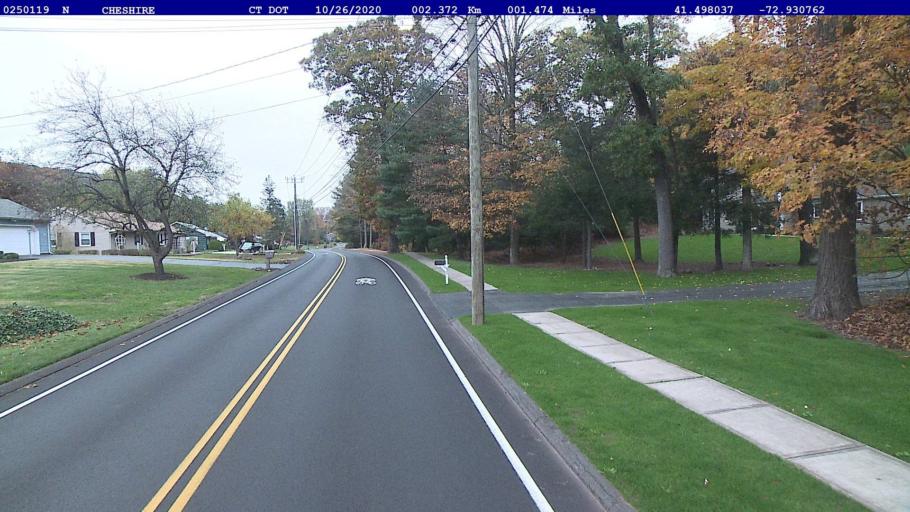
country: US
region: Connecticut
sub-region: New Haven County
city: Cheshire
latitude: 41.4980
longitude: -72.9308
